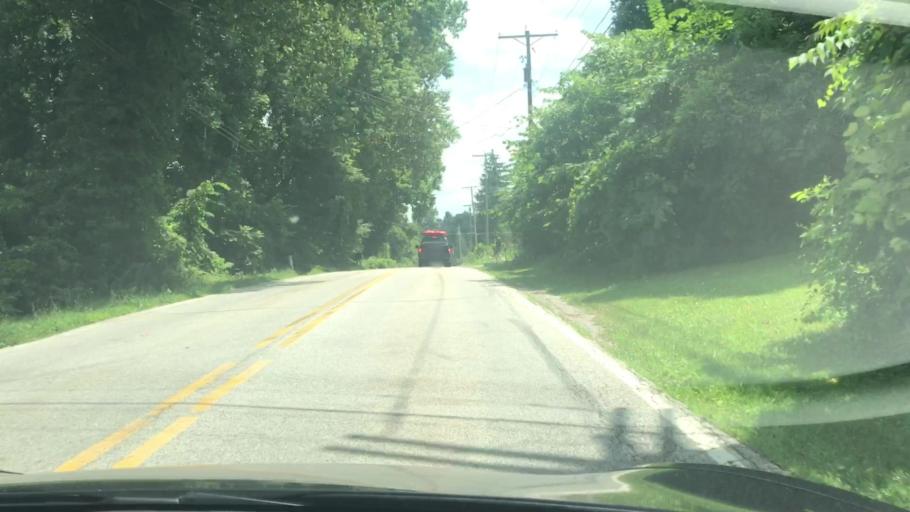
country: US
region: Pennsylvania
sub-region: York County
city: Valley Green
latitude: 40.1156
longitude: -76.7759
